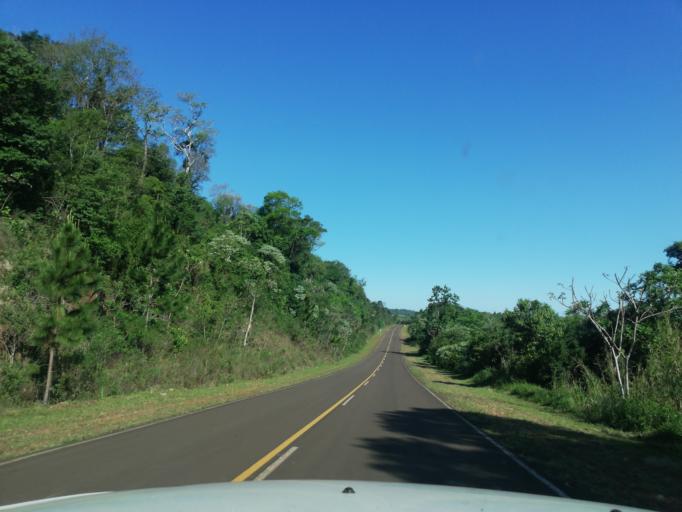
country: AR
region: Misiones
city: Arroyo del Medio
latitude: -27.6557
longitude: -55.4026
